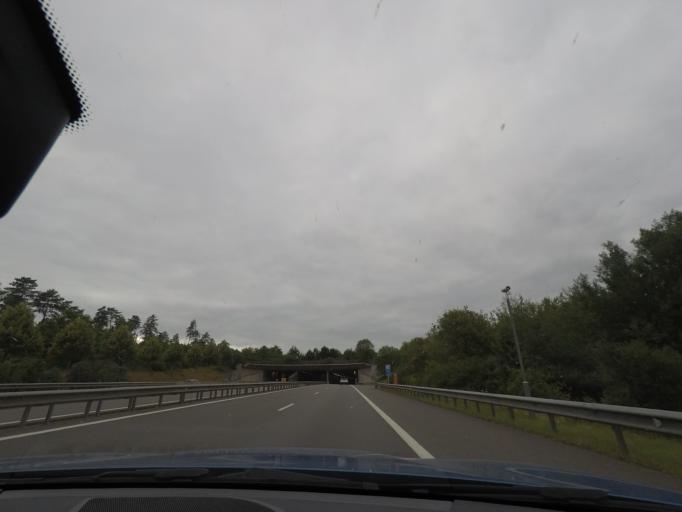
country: LU
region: Luxembourg
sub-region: Canton de Mersch
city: Bissen
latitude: 49.7712
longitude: 6.0867
